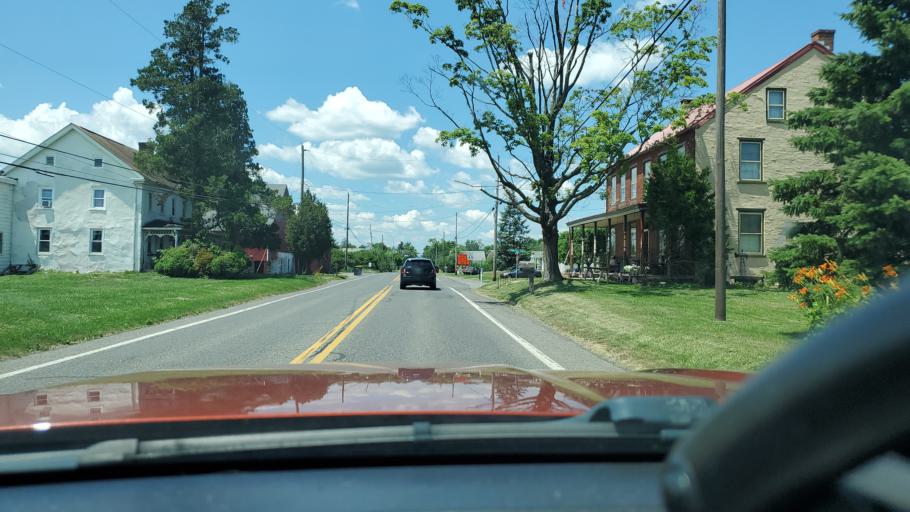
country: US
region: Pennsylvania
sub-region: Montgomery County
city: Gilbertsville
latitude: 40.3079
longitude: -75.5355
